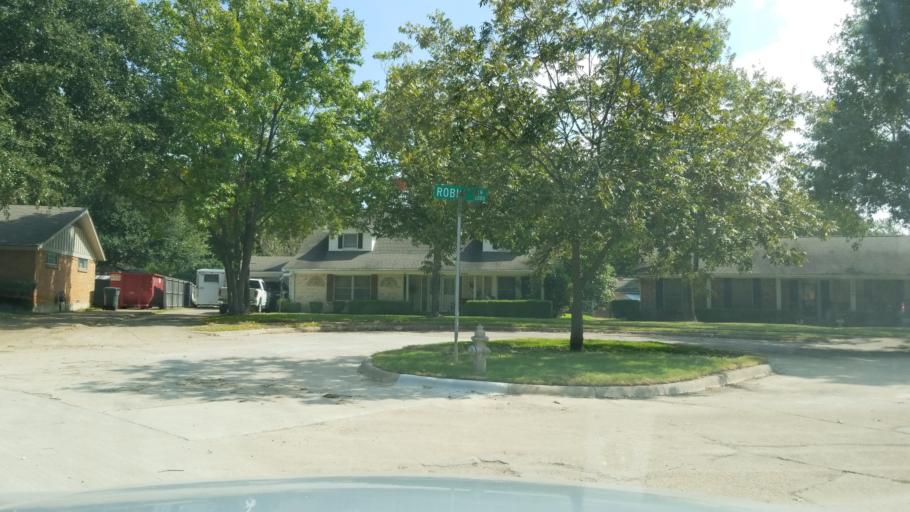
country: US
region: Texas
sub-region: Dallas County
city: Garland
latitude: 32.8930
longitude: -96.6611
